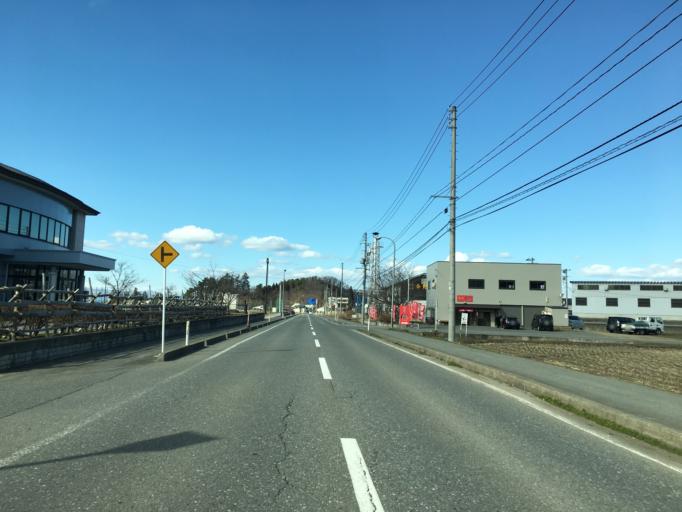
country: JP
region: Yamagata
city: Yonezawa
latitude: 37.9176
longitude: 140.1460
